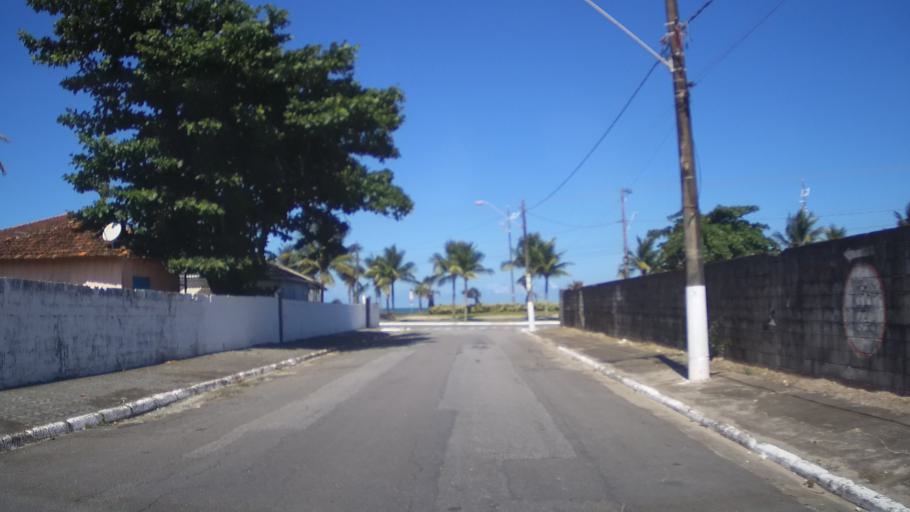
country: BR
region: Sao Paulo
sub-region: Praia Grande
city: Praia Grande
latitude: -24.0381
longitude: -46.4970
